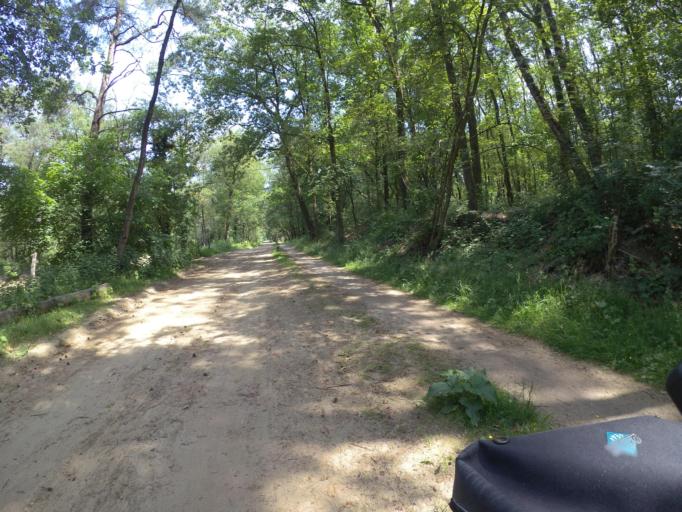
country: NL
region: Overijssel
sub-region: Gemeente Hof van Twente
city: Markelo
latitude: 52.2427
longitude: 6.5264
